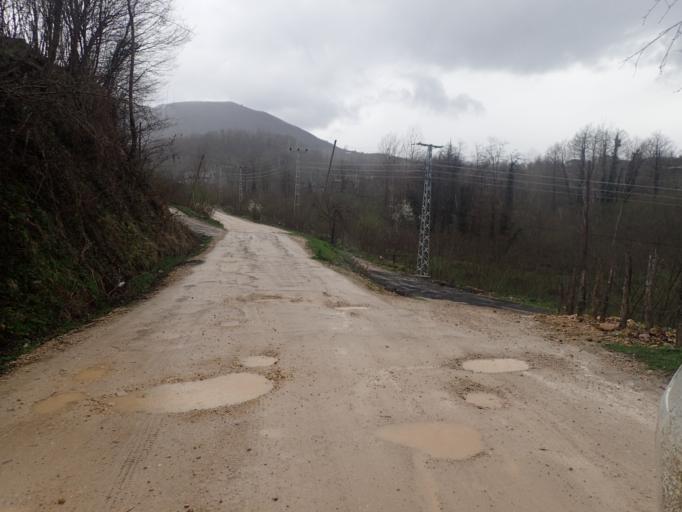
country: TR
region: Ordu
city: Kumru
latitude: 40.9404
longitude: 37.2515
